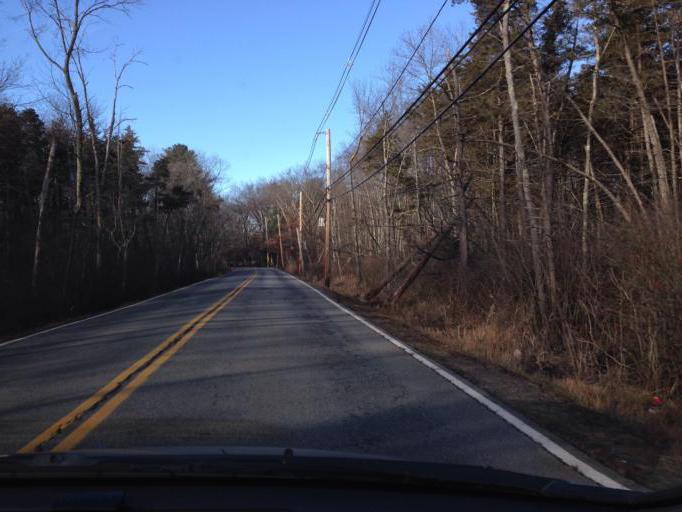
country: US
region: Massachusetts
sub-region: Middlesex County
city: Bedford
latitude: 42.4941
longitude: -71.2962
